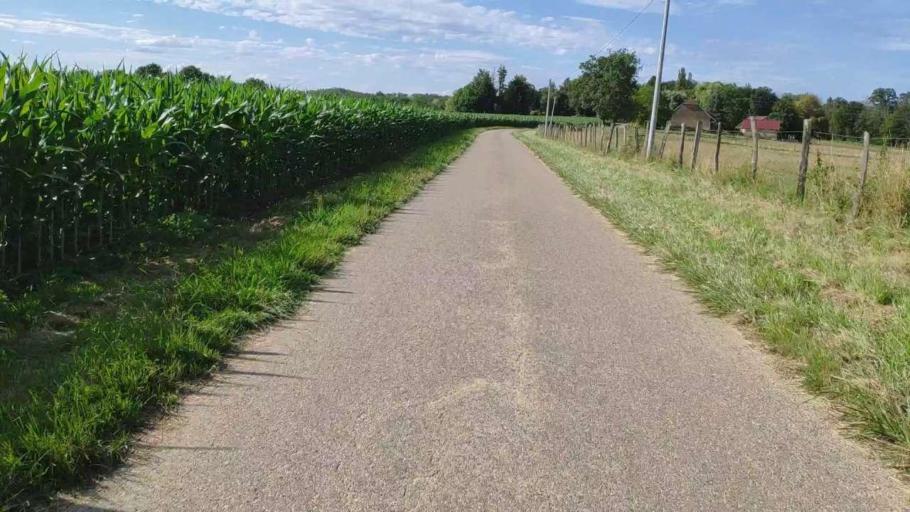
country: FR
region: Franche-Comte
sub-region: Departement du Jura
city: Bletterans
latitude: 46.8111
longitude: 5.4961
